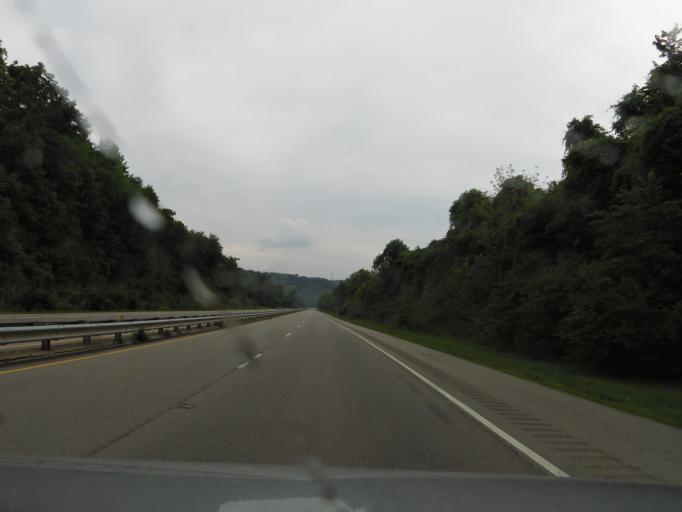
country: US
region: Ohio
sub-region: Brown County
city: Ripley
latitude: 38.7778
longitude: -83.8121
